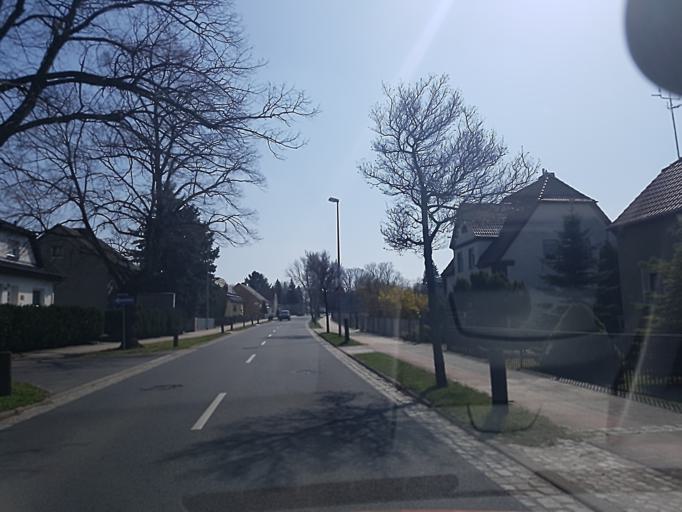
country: DE
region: Brandenburg
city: Tschernitz
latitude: 51.6107
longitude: 14.6059
